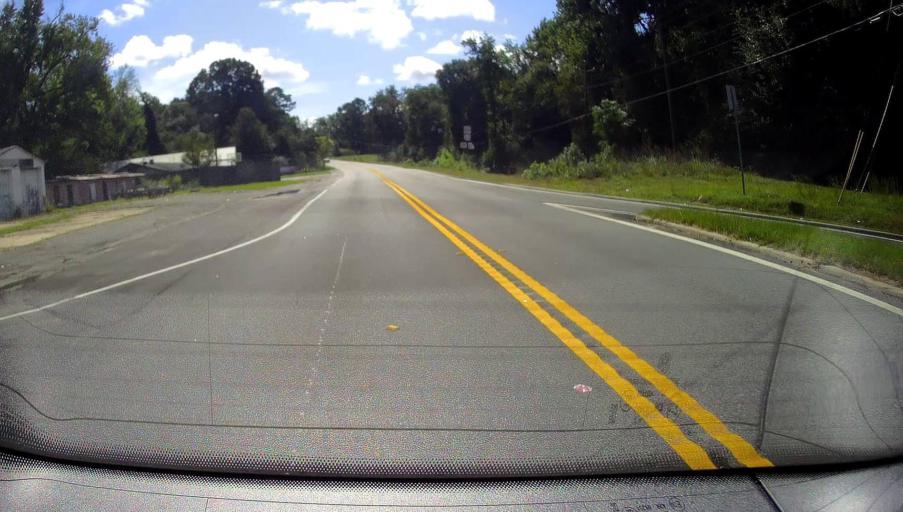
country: US
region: Georgia
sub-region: Bibb County
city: Macon
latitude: 32.8383
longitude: -83.5754
